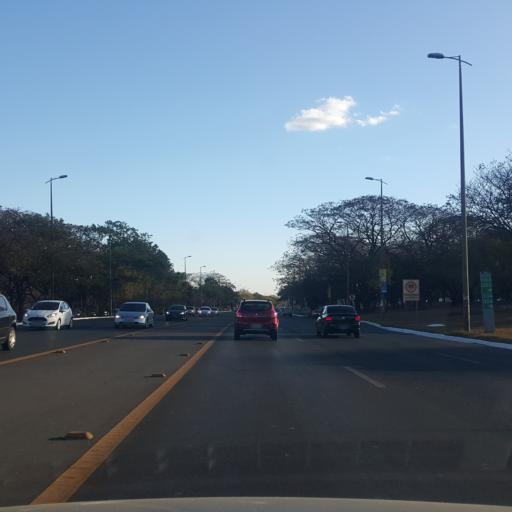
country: BR
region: Federal District
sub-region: Brasilia
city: Brasilia
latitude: -15.8084
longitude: -47.8914
